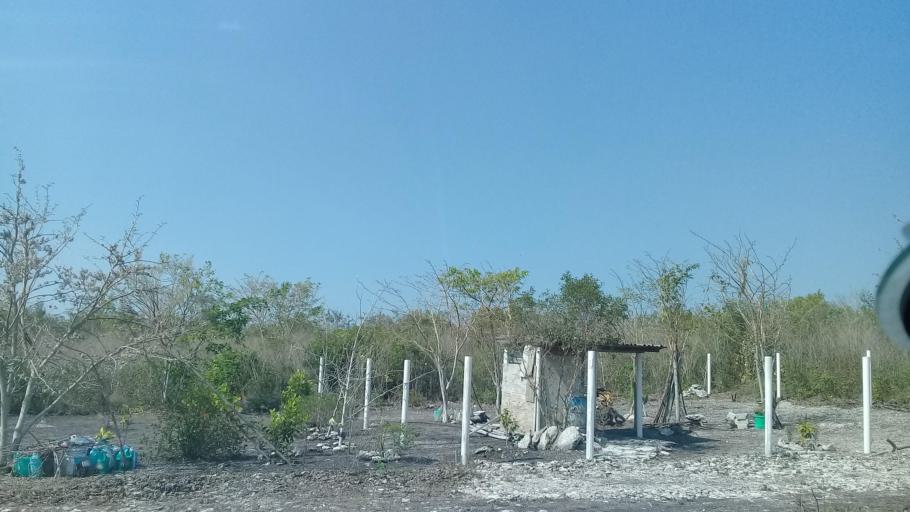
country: MX
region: Veracruz
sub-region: Emiliano Zapata
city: Plan del Rio
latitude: 19.4023
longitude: -96.6156
